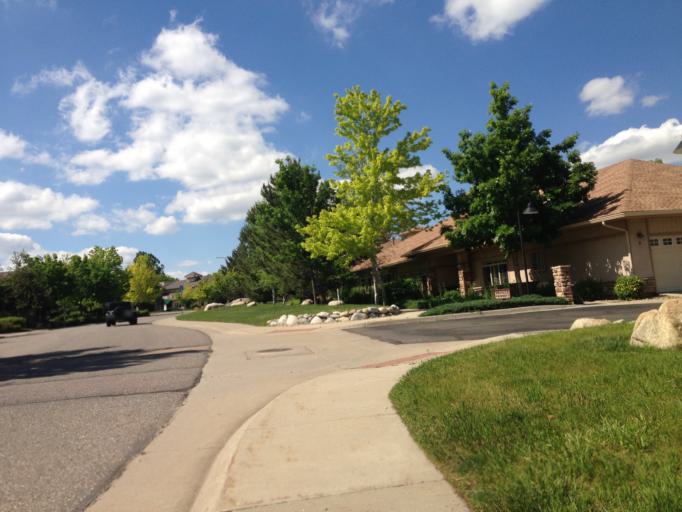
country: US
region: Colorado
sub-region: Boulder County
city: Louisville
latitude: 40.0116
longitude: -105.1282
